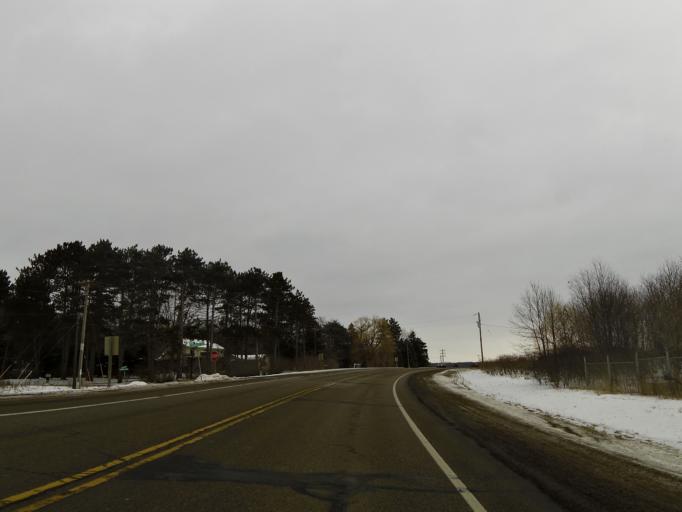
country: US
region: Minnesota
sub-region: Washington County
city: Stillwater
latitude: 45.0713
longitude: -92.7893
